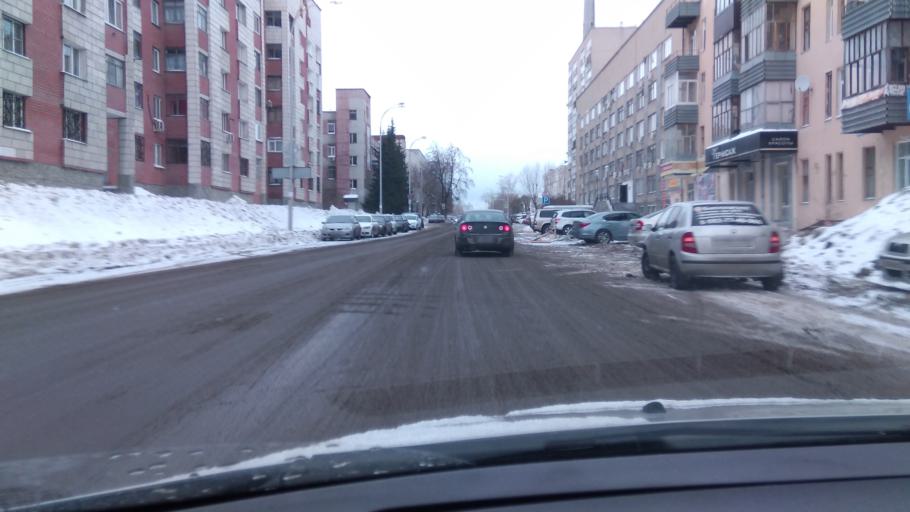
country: RU
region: Sverdlovsk
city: Yekaterinburg
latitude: 56.8186
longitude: 60.6094
